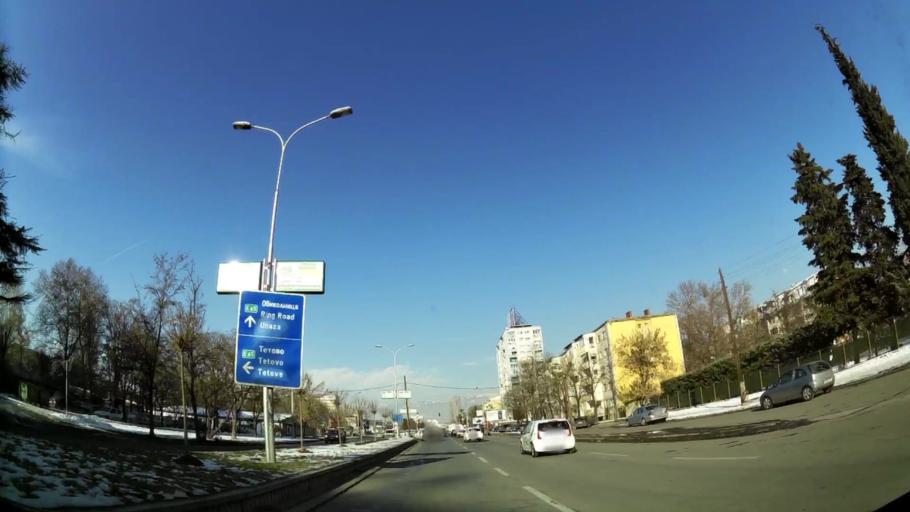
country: MK
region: Karpos
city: Skopje
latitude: 42.0006
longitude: 21.4044
